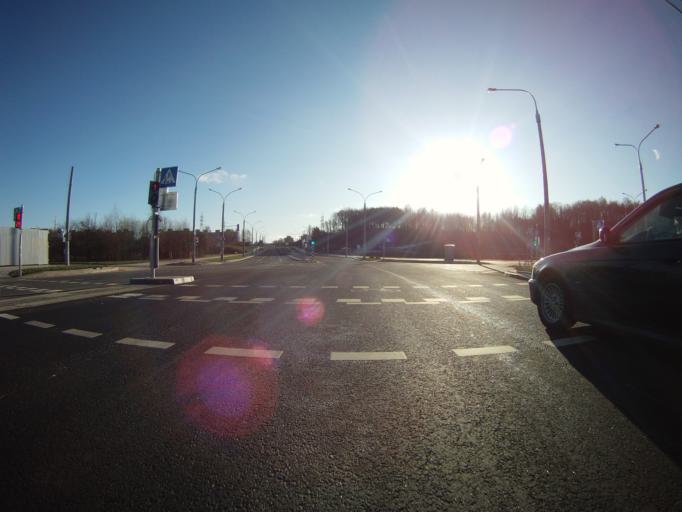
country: BY
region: Minsk
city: Novoye Medvezhino
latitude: 53.8735
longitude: 27.4559
